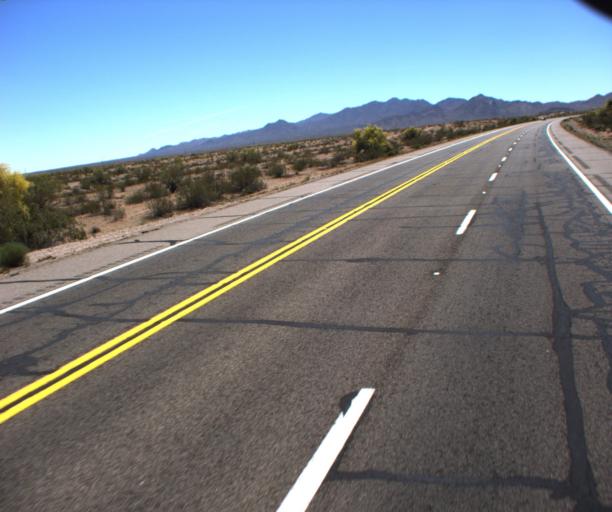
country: US
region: Arizona
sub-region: Mohave County
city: Desert Hills
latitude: 34.7031
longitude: -114.3027
